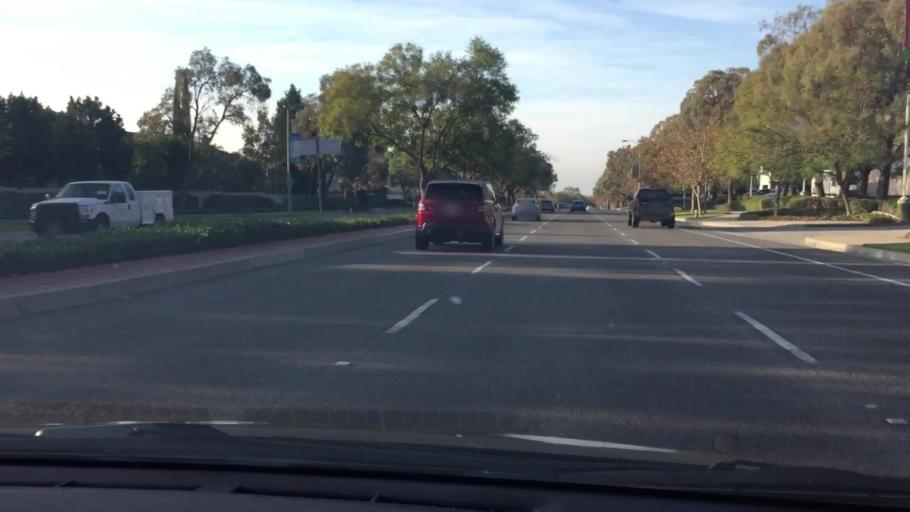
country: US
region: California
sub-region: Orange County
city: Rancho Santa Margarita
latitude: 33.6255
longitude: -117.6071
